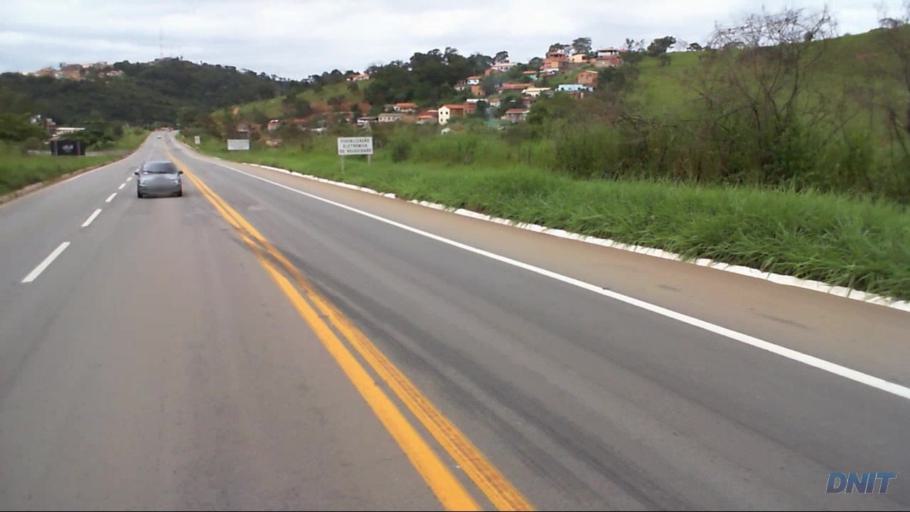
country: BR
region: Minas Gerais
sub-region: Barao De Cocais
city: Barao de Cocais
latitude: -19.8342
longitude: -43.3611
